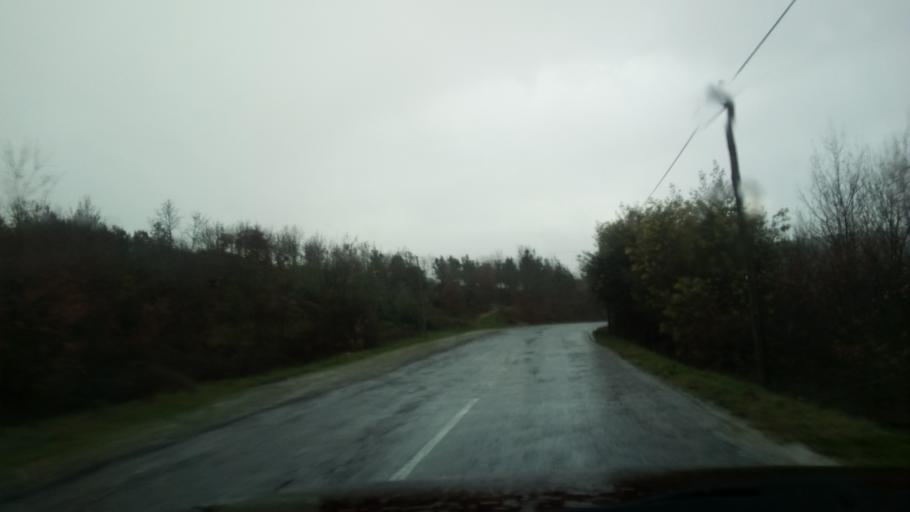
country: PT
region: Guarda
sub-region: Fornos de Algodres
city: Fornos de Algodres
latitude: 40.6255
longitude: -7.4726
